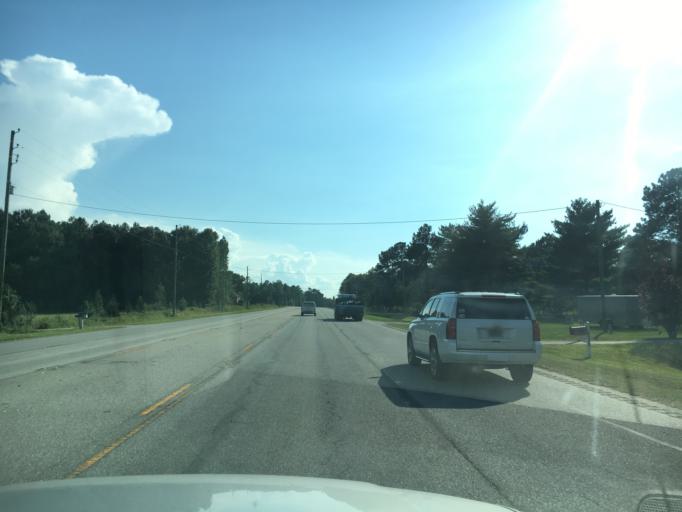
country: US
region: South Carolina
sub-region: Laurens County
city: Clinton
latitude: 34.4273
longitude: -81.9051
